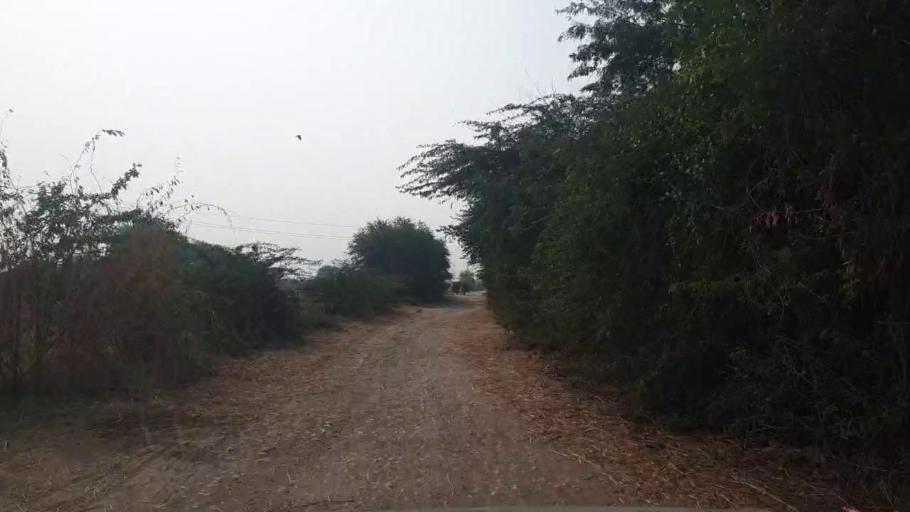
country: PK
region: Sindh
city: Tando Jam
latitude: 25.2873
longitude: 68.4966
